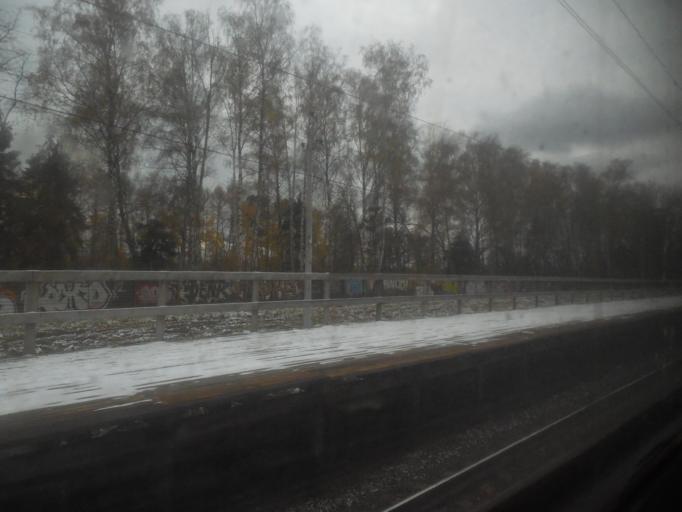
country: RU
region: Moskovskaya
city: Novoivanovskoye
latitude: 55.6977
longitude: 37.3392
